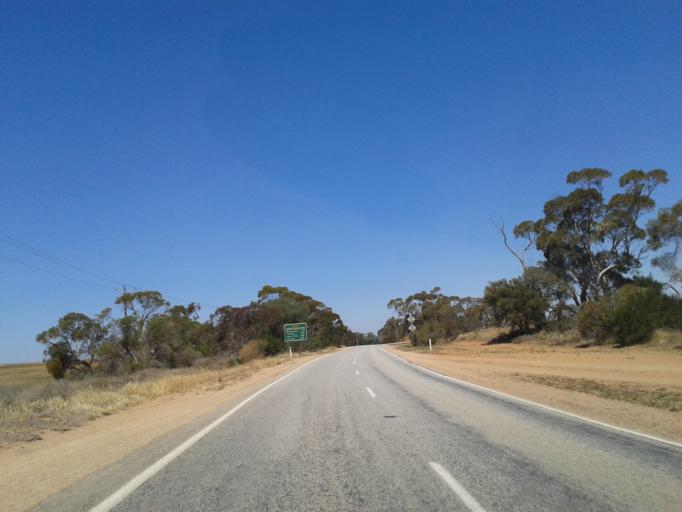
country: AU
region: Victoria
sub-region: Swan Hill
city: Swan Hill
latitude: -34.7226
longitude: 143.1733
